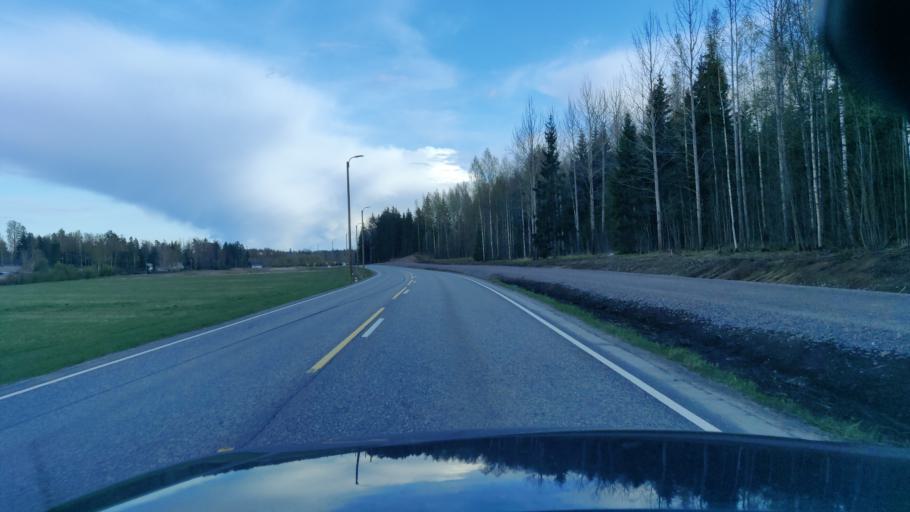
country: FI
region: Uusimaa
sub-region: Helsinki
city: Jaervenpaeae
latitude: 60.4753
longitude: 25.0663
